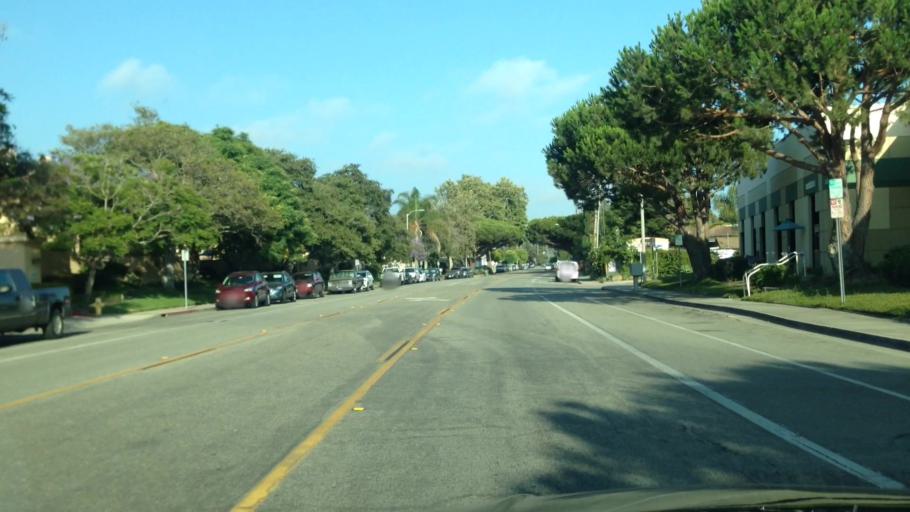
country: US
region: California
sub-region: Santa Barbara County
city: Carpinteria
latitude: 34.4039
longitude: -119.5337
